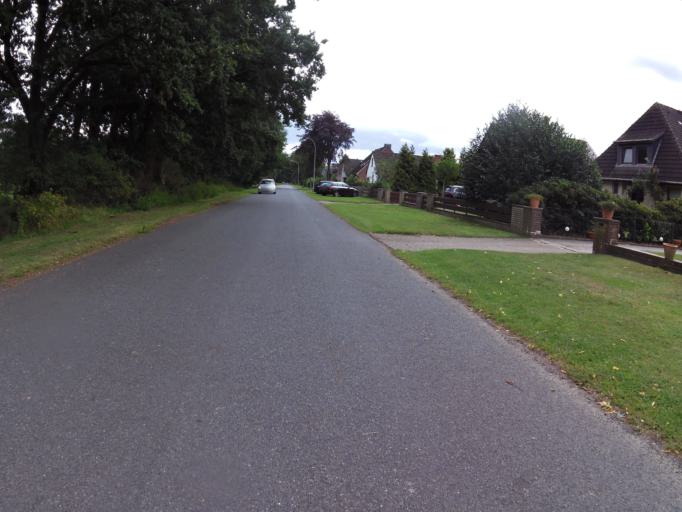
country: DE
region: Lower Saxony
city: Lunestedt
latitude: 53.4927
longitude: 8.7238
